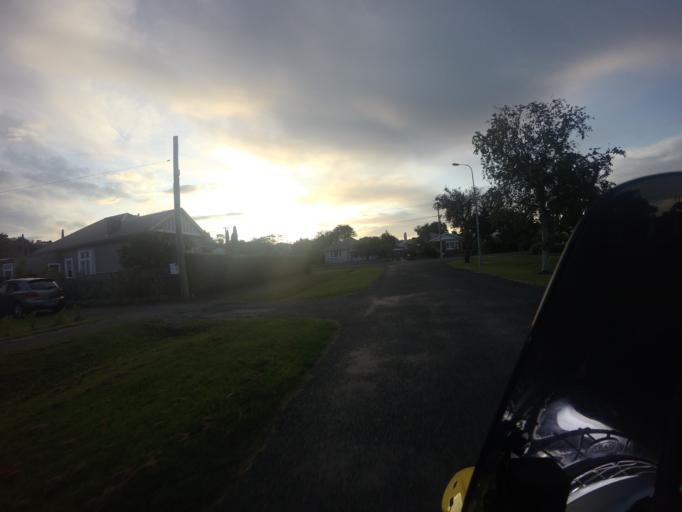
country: NZ
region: Gisborne
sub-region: Gisborne District
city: Gisborne
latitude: -38.6632
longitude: 178.0358
